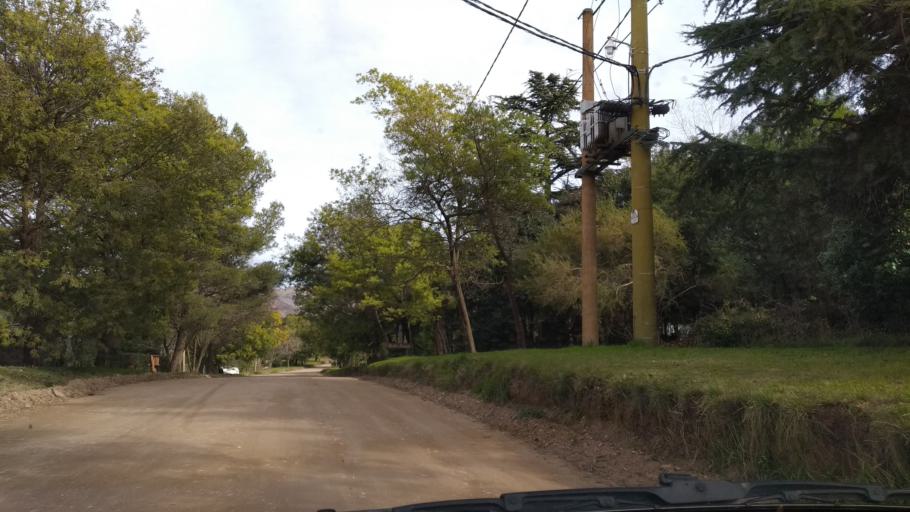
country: AR
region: Buenos Aires
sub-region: Partido de Tornquist
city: Tornquist
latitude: -38.0846
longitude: -61.9294
